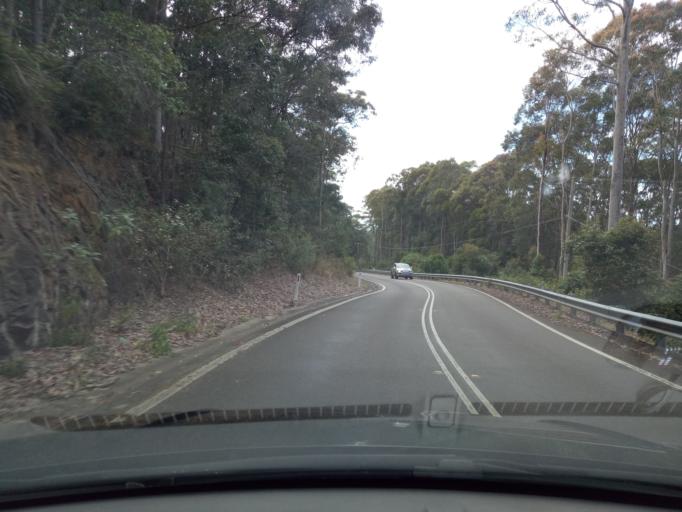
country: AU
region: New South Wales
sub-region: Gosford Shire
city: Holgate
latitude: -33.3831
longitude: 151.4305
